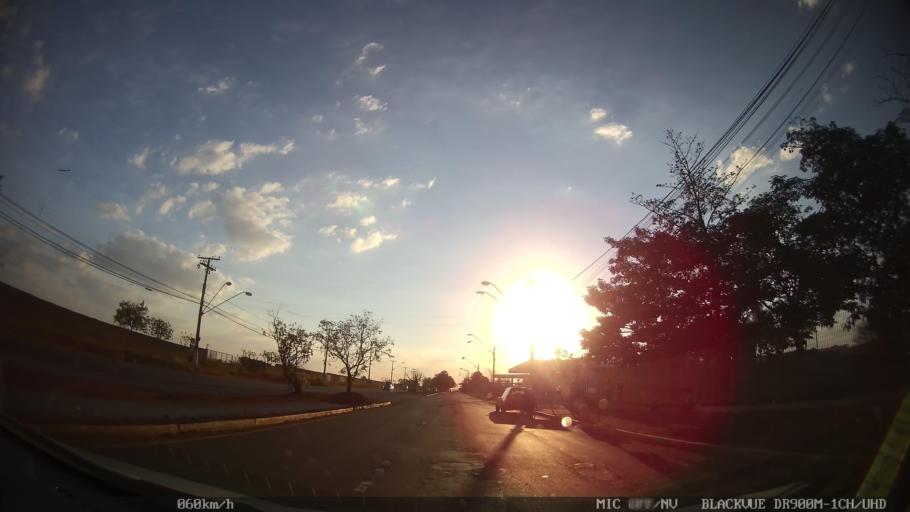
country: BR
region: Sao Paulo
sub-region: Ribeirao Preto
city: Ribeirao Preto
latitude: -21.1476
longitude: -47.7638
